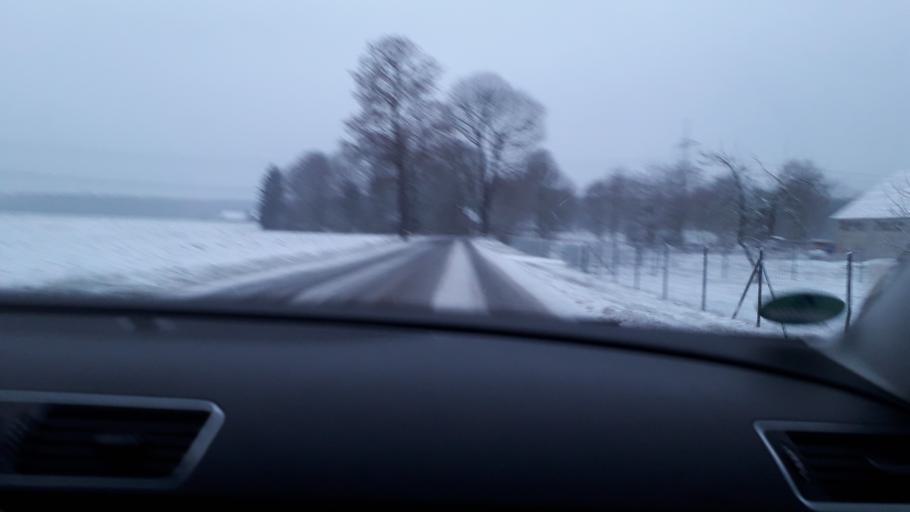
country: DE
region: Brandenburg
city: Spremberg
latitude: 51.5964
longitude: 14.4460
